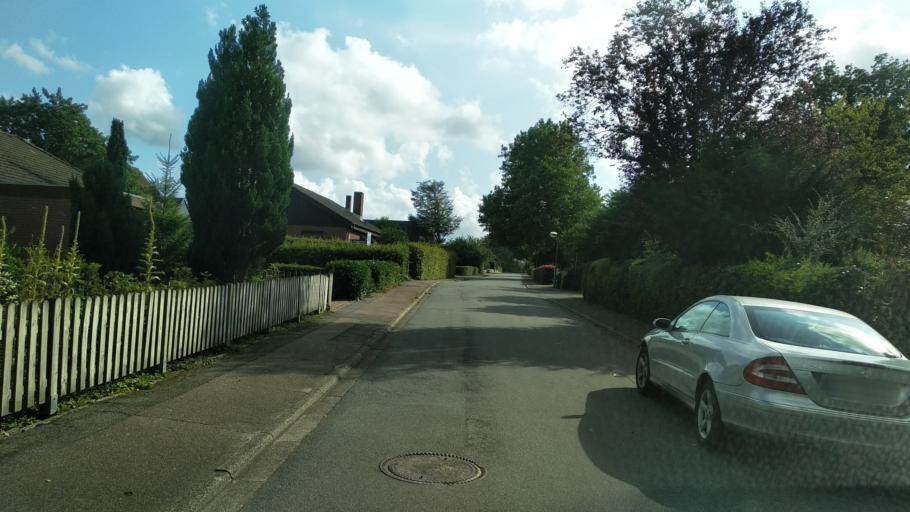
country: DE
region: Schleswig-Holstein
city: Neuberend
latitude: 54.5510
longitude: 9.5285
